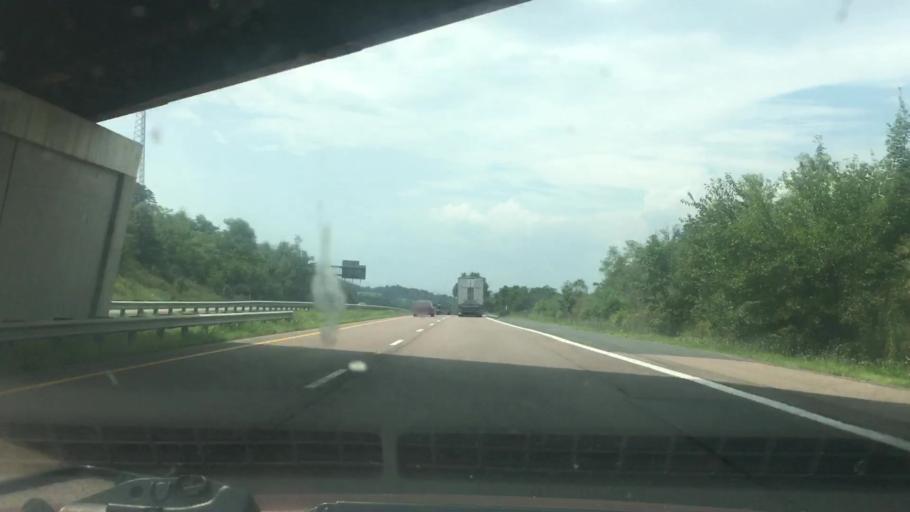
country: US
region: Maryland
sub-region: Allegany County
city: Cumberland
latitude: 39.7035
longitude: -78.6308
